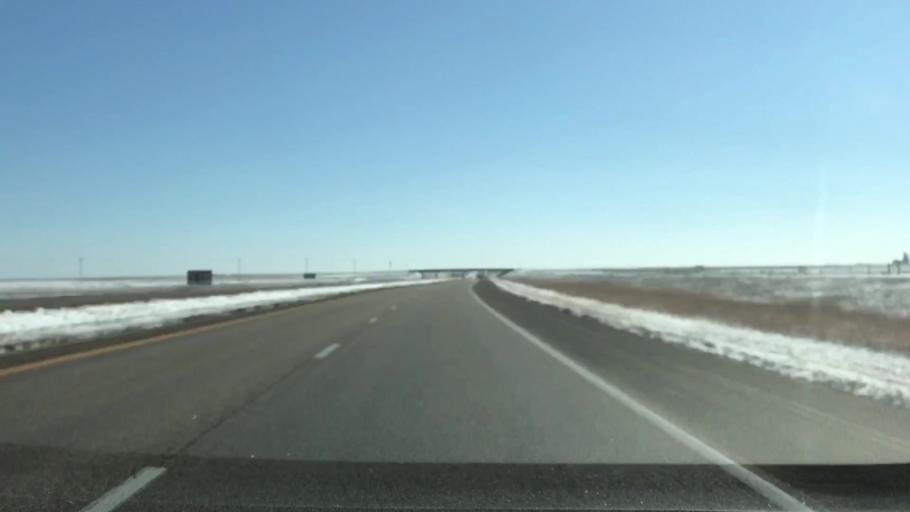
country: US
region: Kansas
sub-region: Thomas County
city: Colby
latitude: 39.3068
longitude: -100.9654
